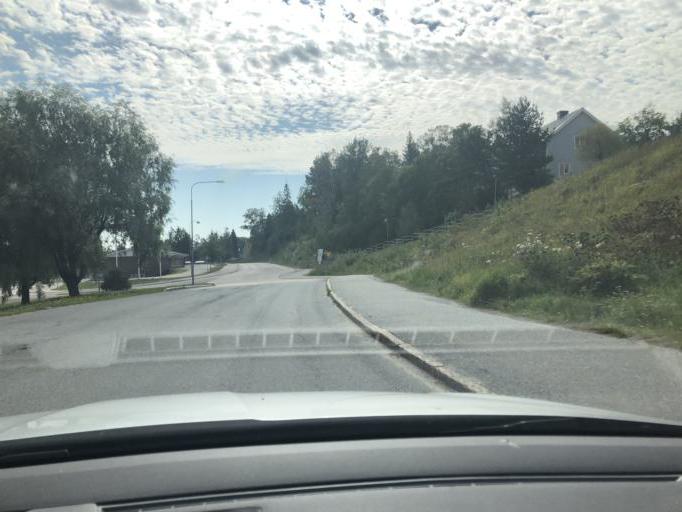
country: SE
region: Vaesternorrland
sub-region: Kramfors Kommun
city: Kramfors
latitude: 62.9282
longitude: 17.7784
